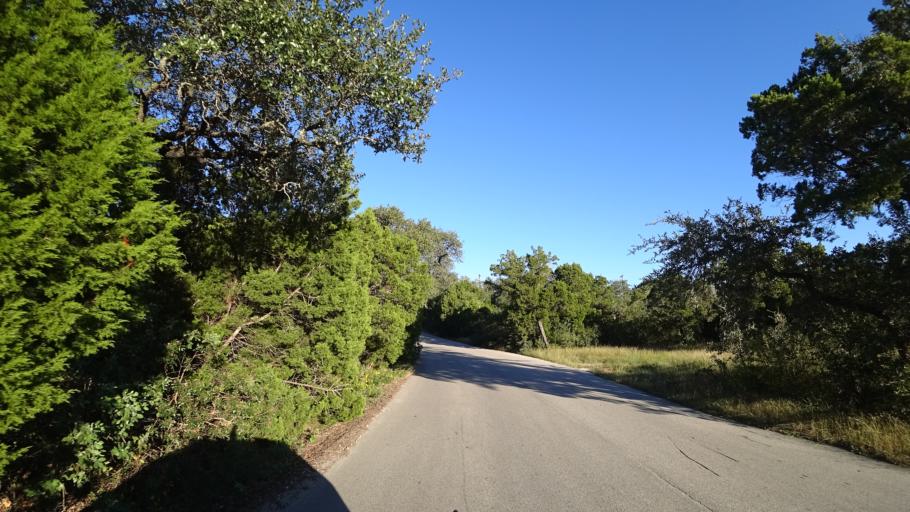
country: US
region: Texas
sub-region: Travis County
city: West Lake Hills
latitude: 30.3349
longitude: -97.8147
